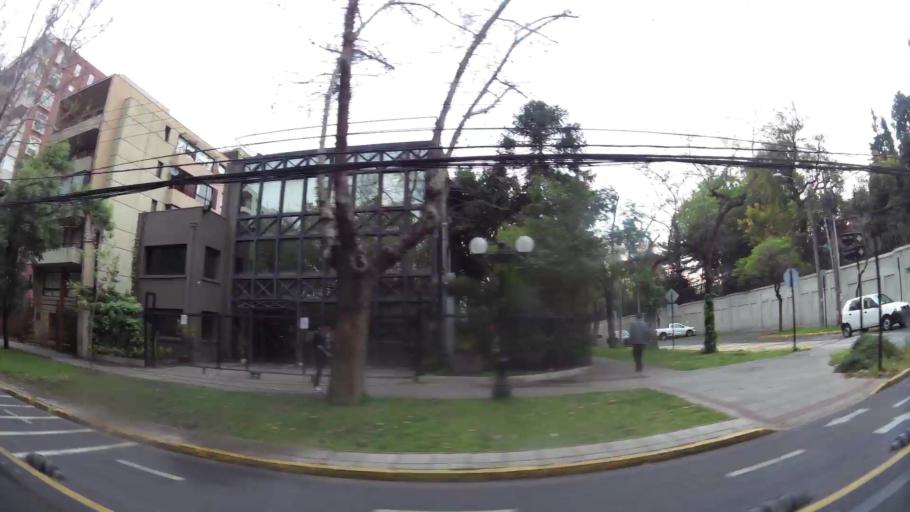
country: CL
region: Santiago Metropolitan
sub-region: Provincia de Santiago
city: Santiago
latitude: -33.4420
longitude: -70.6179
